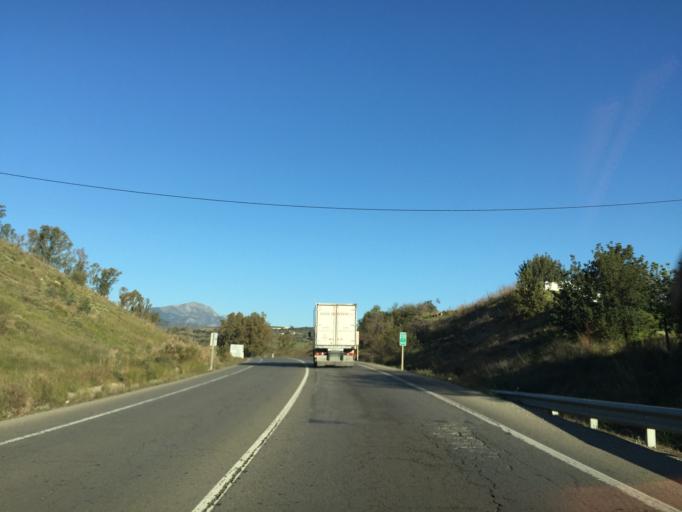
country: ES
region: Andalusia
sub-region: Provincia de Malaga
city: Pizarra
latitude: 36.7669
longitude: -4.7326
